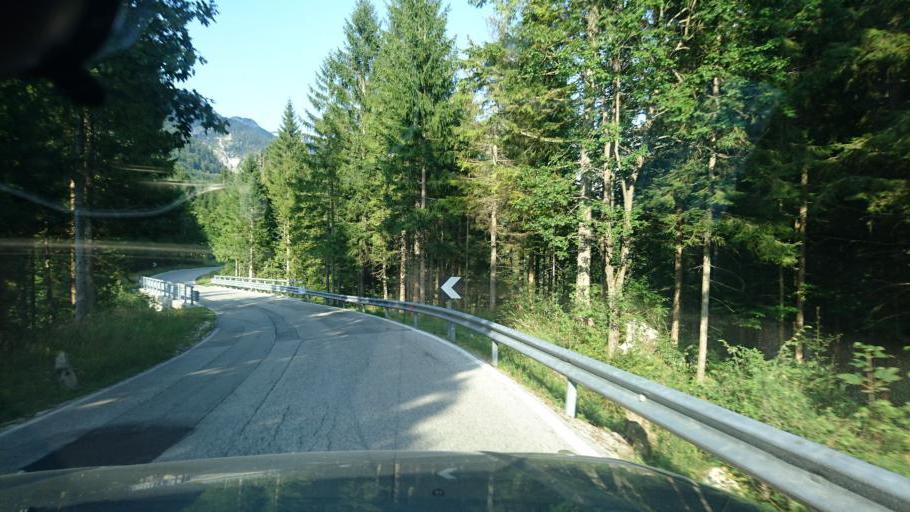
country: SI
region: Bovec
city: Bovec
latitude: 46.3968
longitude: 13.5019
